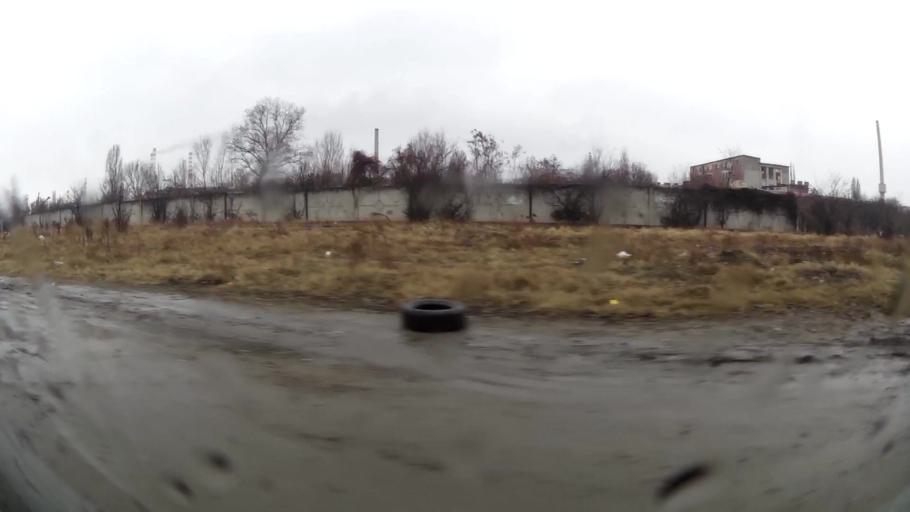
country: BG
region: Sofia-Capital
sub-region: Stolichna Obshtina
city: Sofia
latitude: 42.6607
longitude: 23.4208
